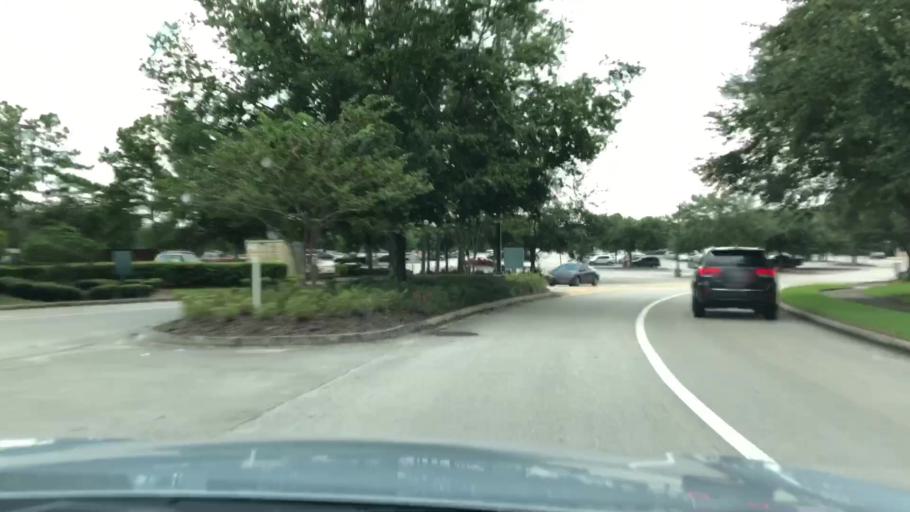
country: US
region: Florida
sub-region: Duval County
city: Jacksonville
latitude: 30.2614
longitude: -81.5542
